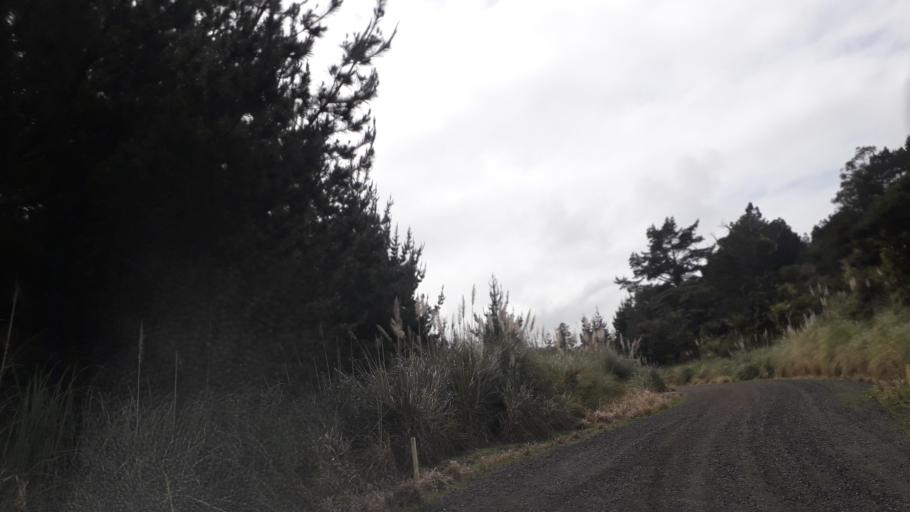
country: NZ
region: Northland
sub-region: Far North District
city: Kaitaia
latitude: -35.3703
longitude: 173.4116
